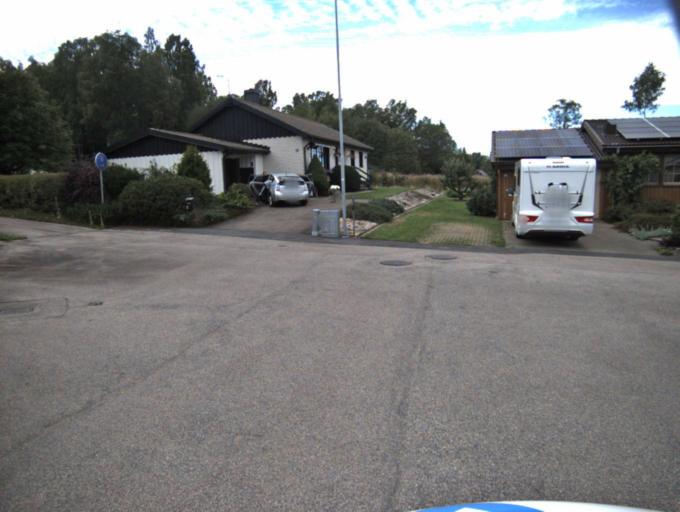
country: SE
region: Vaestra Goetaland
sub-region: Ulricehamns Kommun
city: Ulricehamn
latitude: 57.8619
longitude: 13.4203
